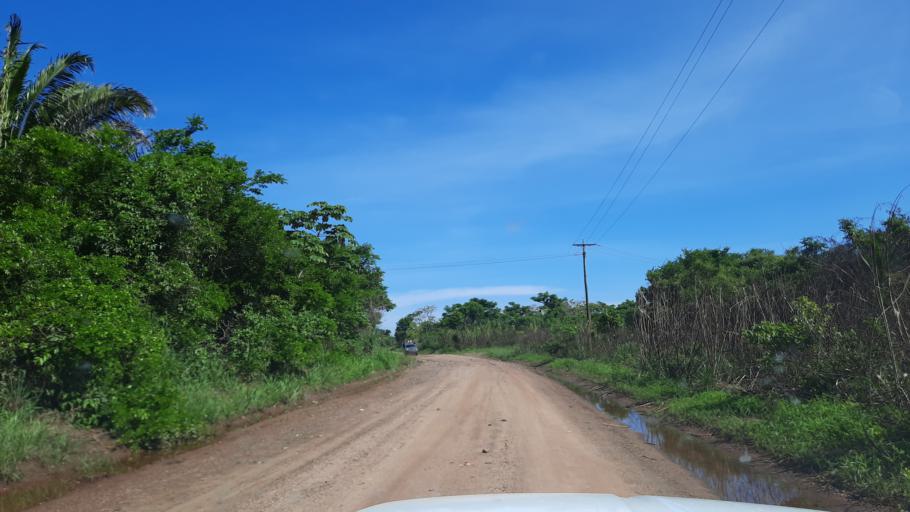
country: BZ
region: Stann Creek
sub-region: Dangriga
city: Dangriga
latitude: 17.1601
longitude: -88.3287
